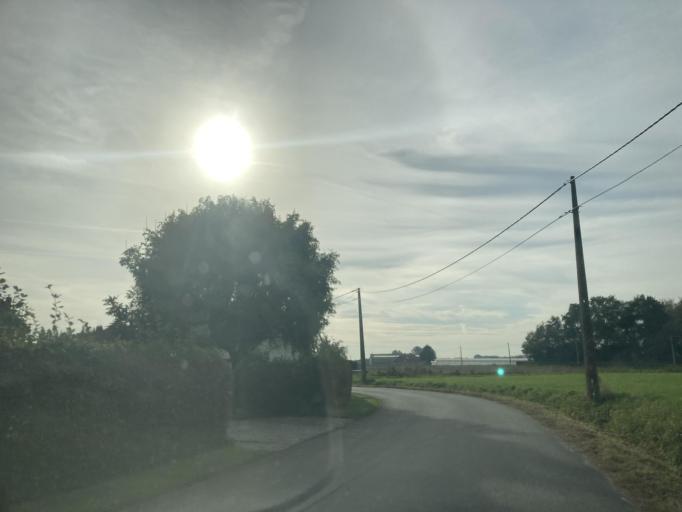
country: BE
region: Flanders
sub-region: Provincie West-Vlaanderen
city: Wervik
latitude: 50.8107
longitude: 3.0562
